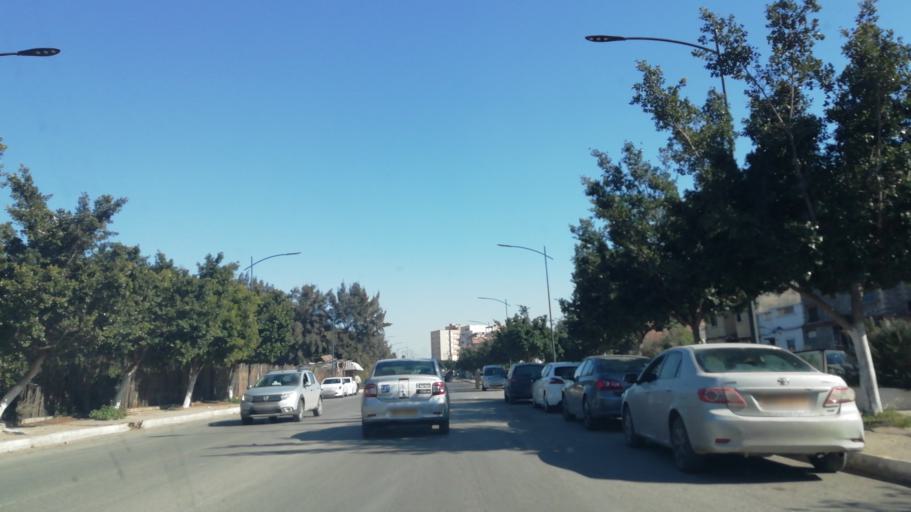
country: DZ
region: Oran
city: Bir el Djir
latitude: 35.7162
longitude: -0.5859
